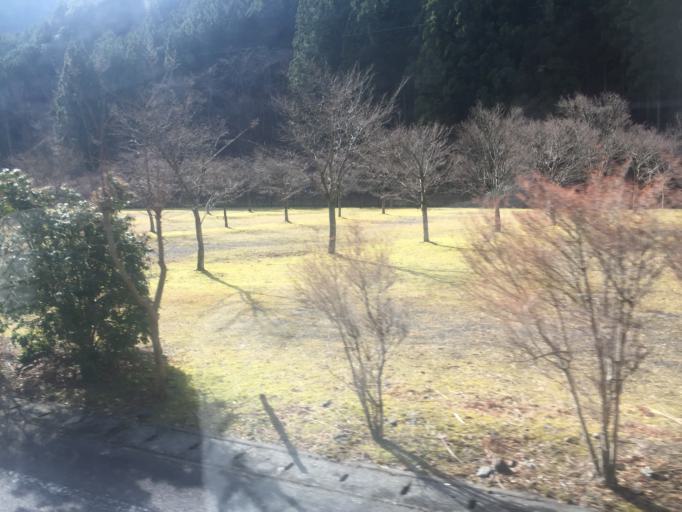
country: JP
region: Shizuoka
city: Shizuoka-shi
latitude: 35.1769
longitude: 138.1259
